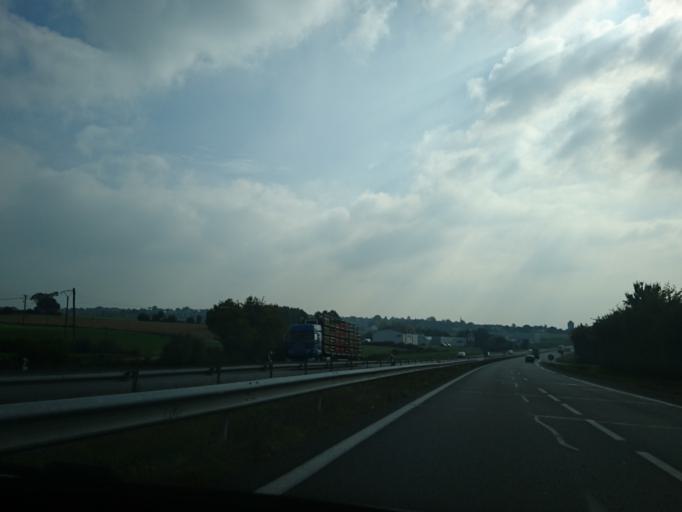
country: FR
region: Brittany
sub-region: Departement d'Ille-et-Vilaine
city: Pance
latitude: 47.8978
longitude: -1.6863
